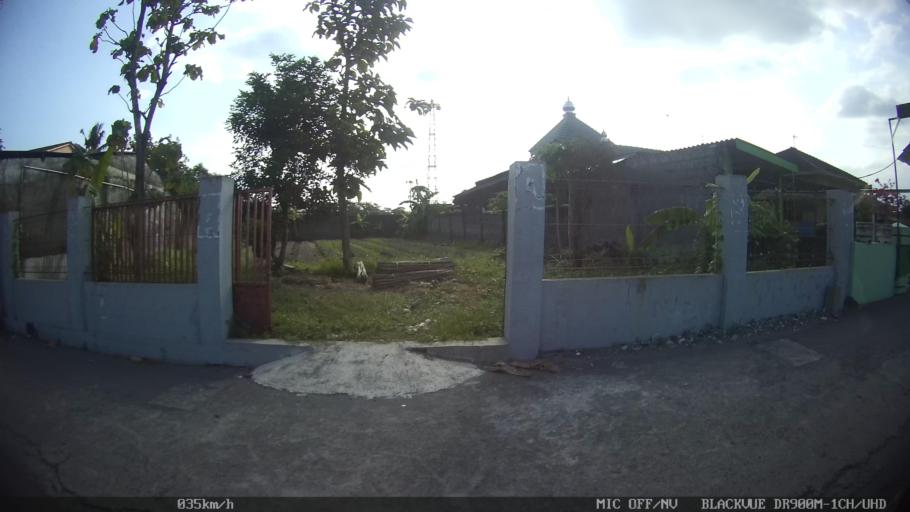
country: ID
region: Central Java
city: Candi Prambanan
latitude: -7.7237
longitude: 110.4723
